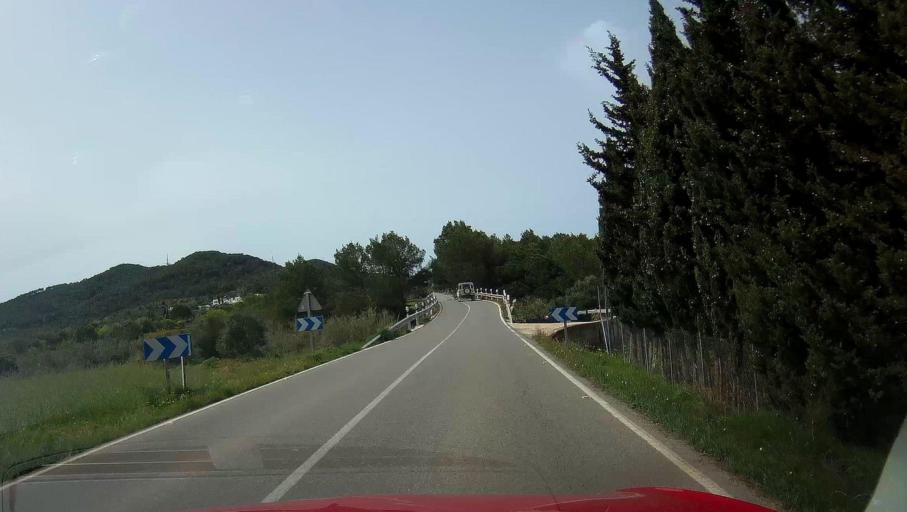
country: ES
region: Balearic Islands
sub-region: Illes Balears
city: Santa Eularia des Riu
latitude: 38.9868
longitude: 1.4902
